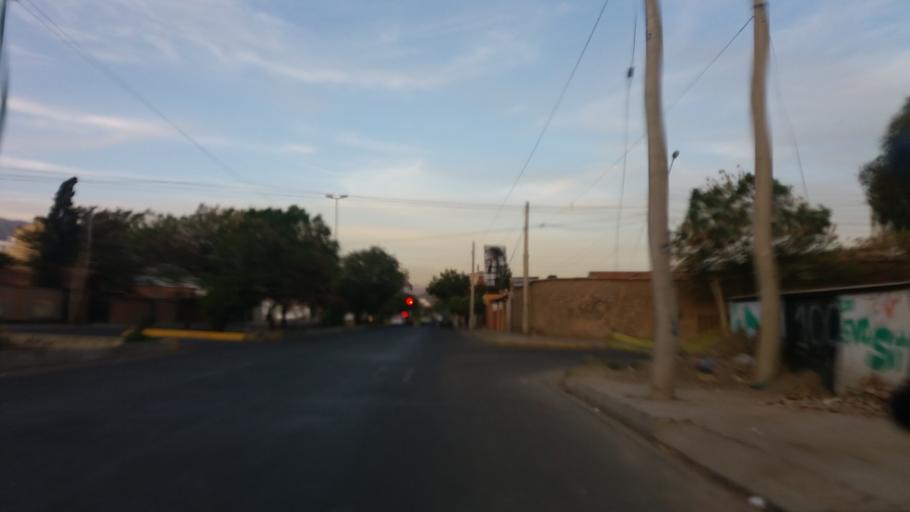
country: BO
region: Cochabamba
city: Cochabamba
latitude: -17.3831
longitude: -66.1831
